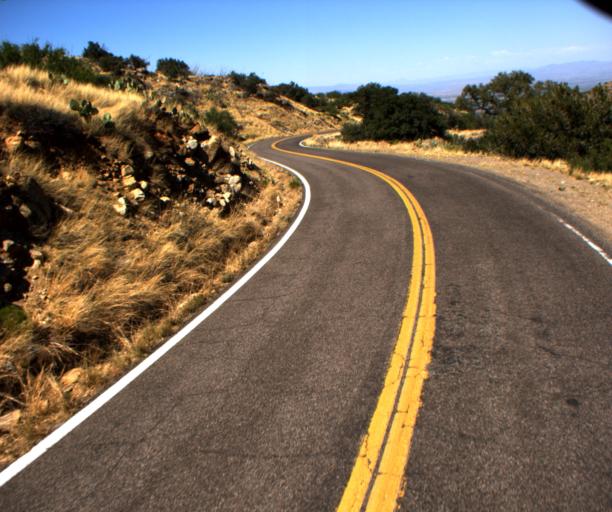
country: US
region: Arizona
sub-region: Graham County
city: Swift Trail Junction
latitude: 32.6727
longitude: -109.7836
